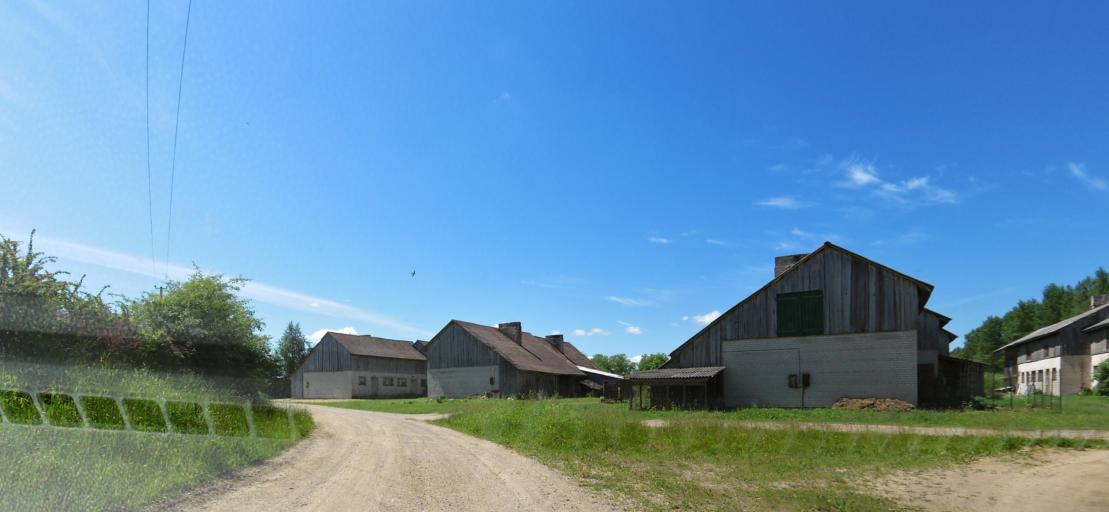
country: LT
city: Moletai
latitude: 55.0766
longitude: 25.2522
